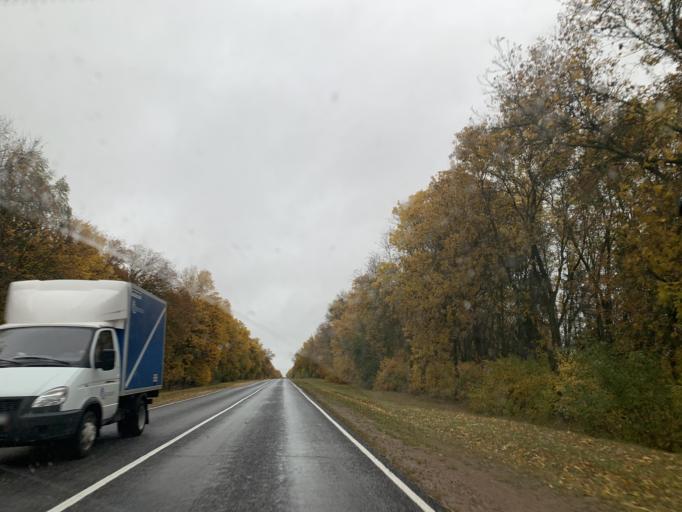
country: BY
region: Minsk
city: Novy Svyerzhan'
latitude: 53.4366
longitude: 26.6516
